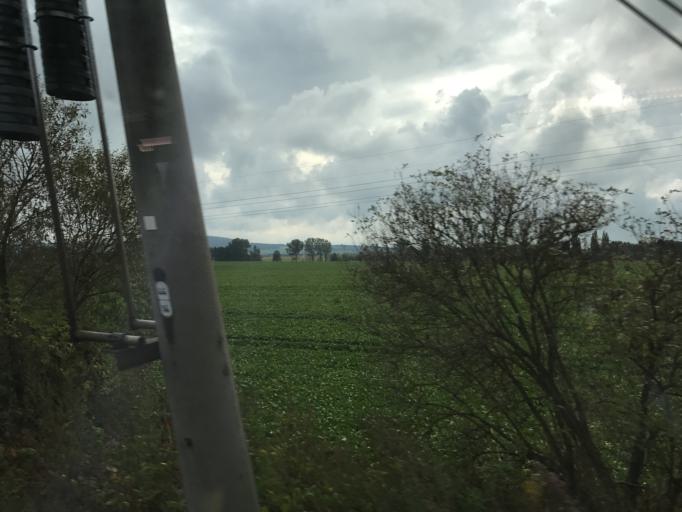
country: DE
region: Saxony
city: Dahlen
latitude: 51.3477
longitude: 12.9984
